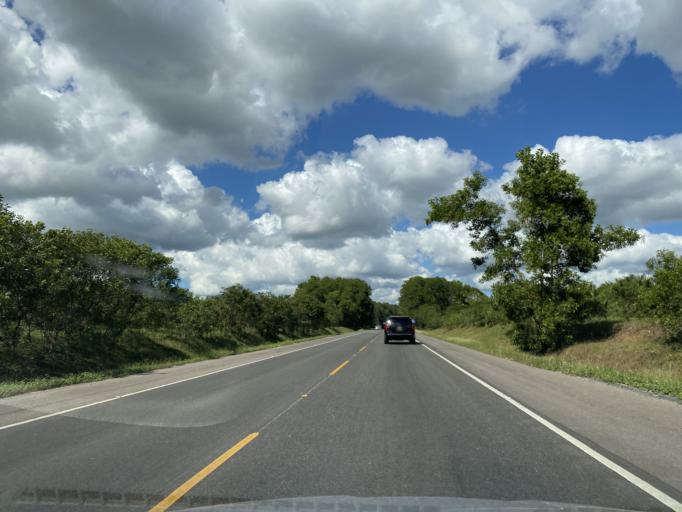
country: DO
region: Monte Plata
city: Monte Plata
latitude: 18.7463
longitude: -69.7653
